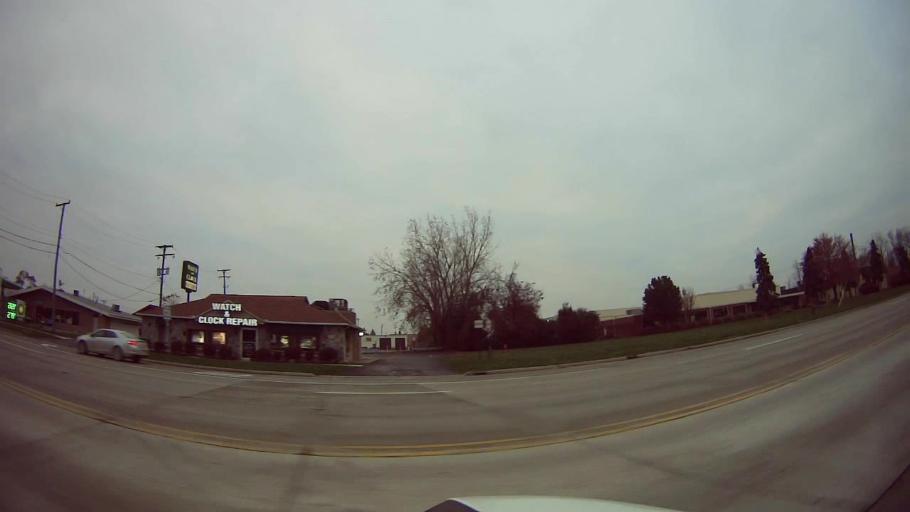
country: US
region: Michigan
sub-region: Oakland County
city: Clawson
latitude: 42.5493
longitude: -83.1088
